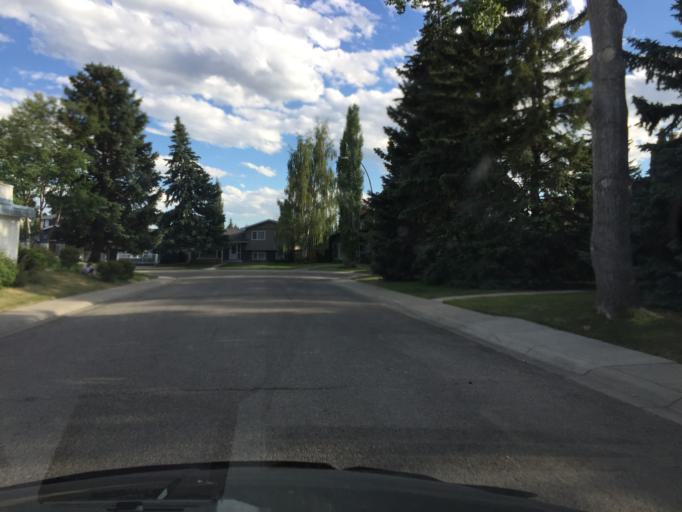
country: CA
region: Alberta
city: Calgary
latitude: 50.9338
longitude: -114.0456
